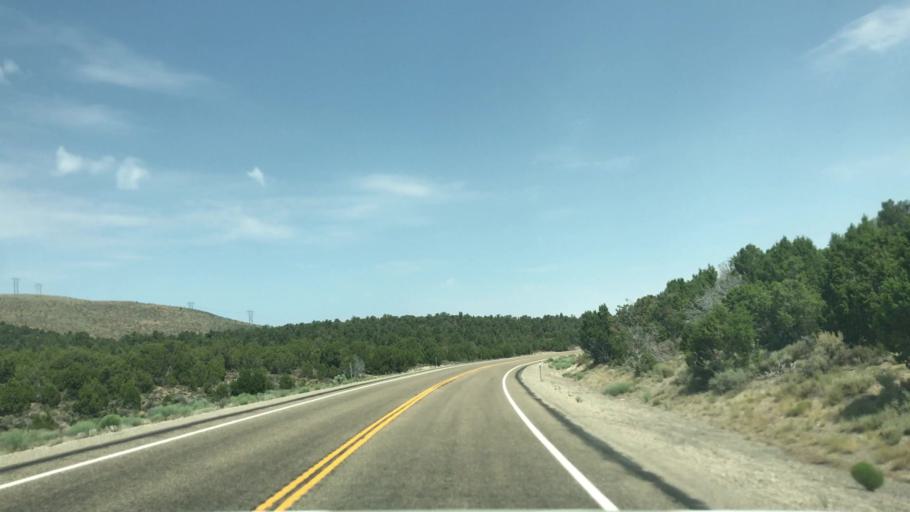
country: US
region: Nevada
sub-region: White Pine County
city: Ely
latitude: 39.3942
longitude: -115.0830
